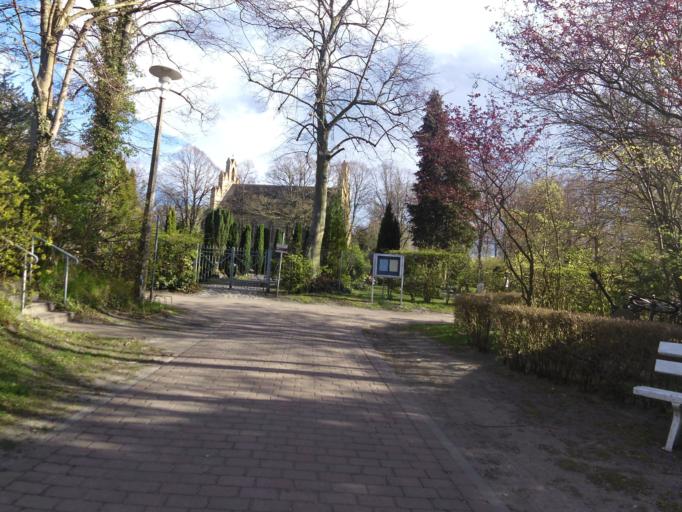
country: DE
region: Mecklenburg-Vorpommern
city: Zingst
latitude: 54.4383
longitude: 12.6886
